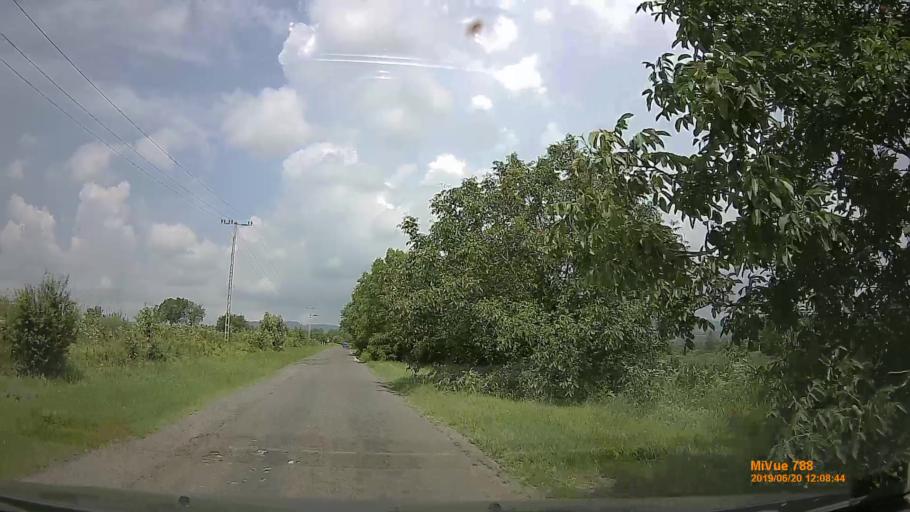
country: HU
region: Baranya
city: Hosszuheteny
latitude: 46.1302
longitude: 18.3668
